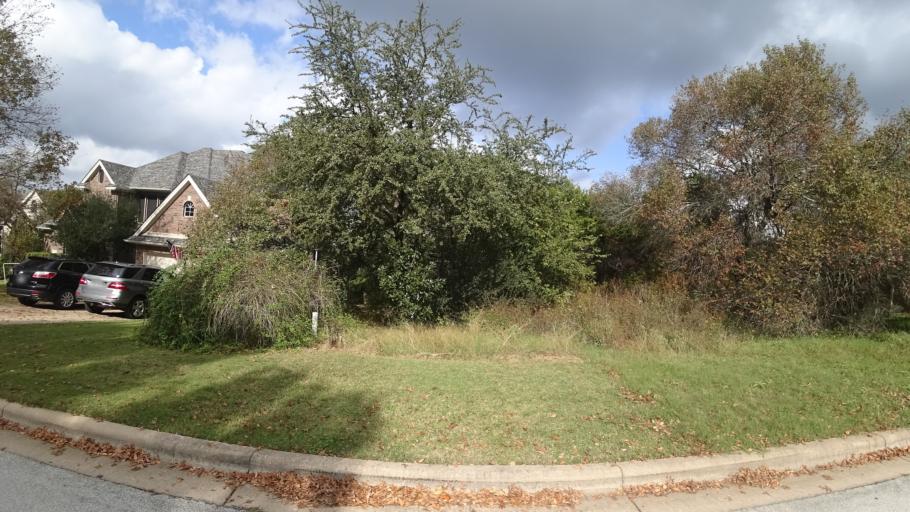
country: US
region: Texas
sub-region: Travis County
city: Barton Creek
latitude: 30.3021
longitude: -97.8938
